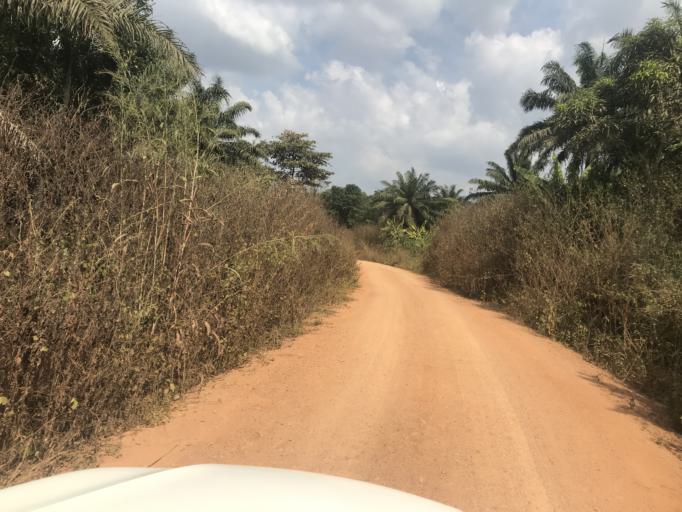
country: NG
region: Osun
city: Inisa
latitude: 7.8760
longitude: 4.3844
